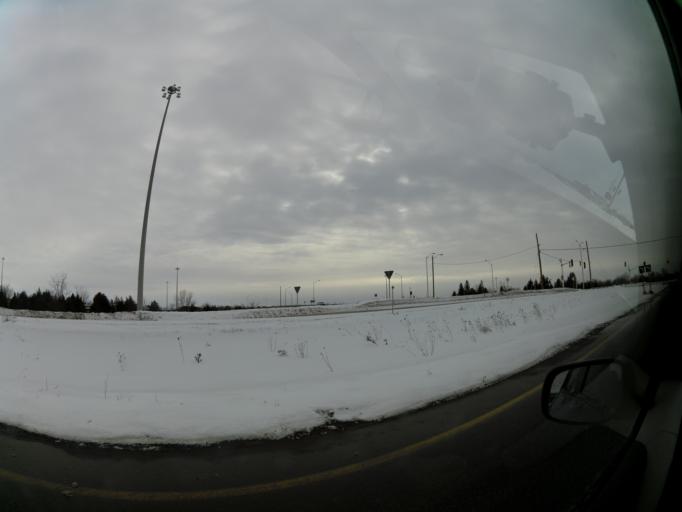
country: CA
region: Ontario
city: Bells Corners
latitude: 45.2955
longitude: -75.9386
